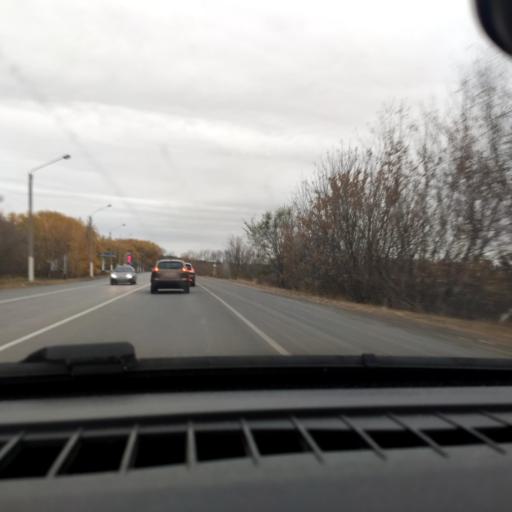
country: RU
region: Voronezj
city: Devitsa
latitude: 51.5980
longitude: 38.9740
